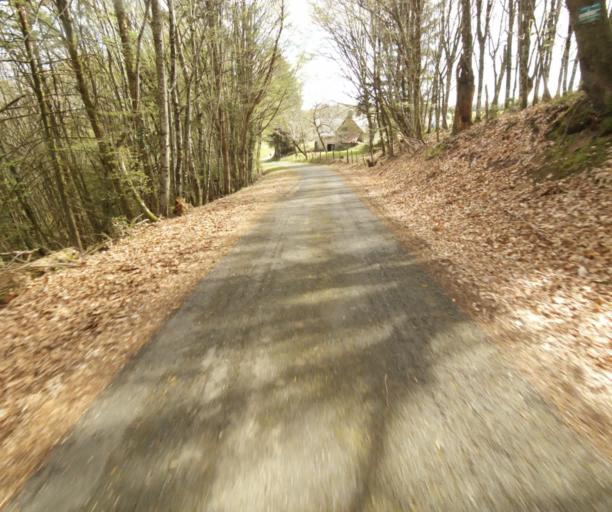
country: FR
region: Limousin
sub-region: Departement de la Correze
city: Laguenne
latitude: 45.2571
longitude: 1.8093
